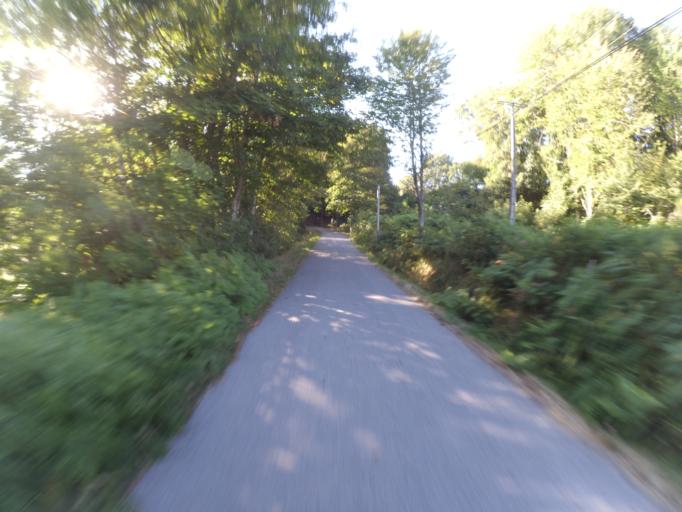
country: FR
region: Limousin
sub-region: Departement de la Creuse
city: Banize
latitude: 45.7699
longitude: 2.0165
